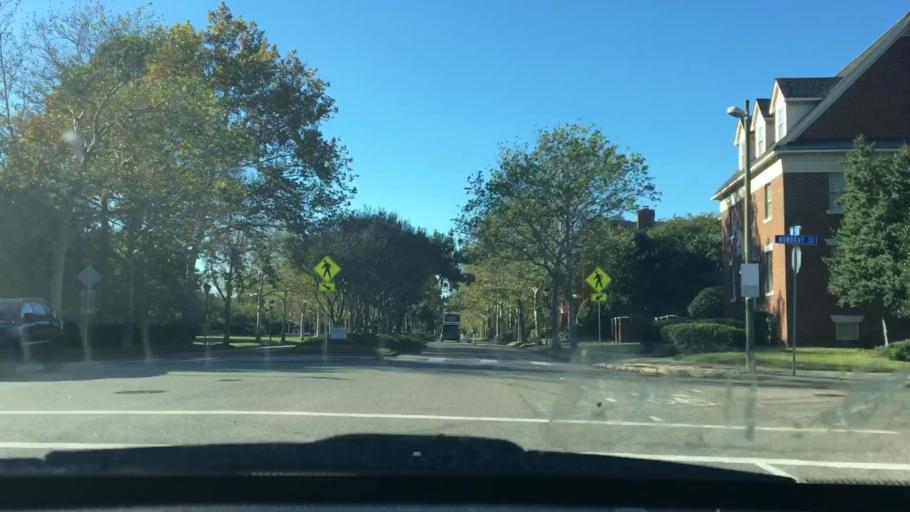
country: US
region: Virginia
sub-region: City of Norfolk
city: Norfolk
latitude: 36.8574
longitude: -76.2931
